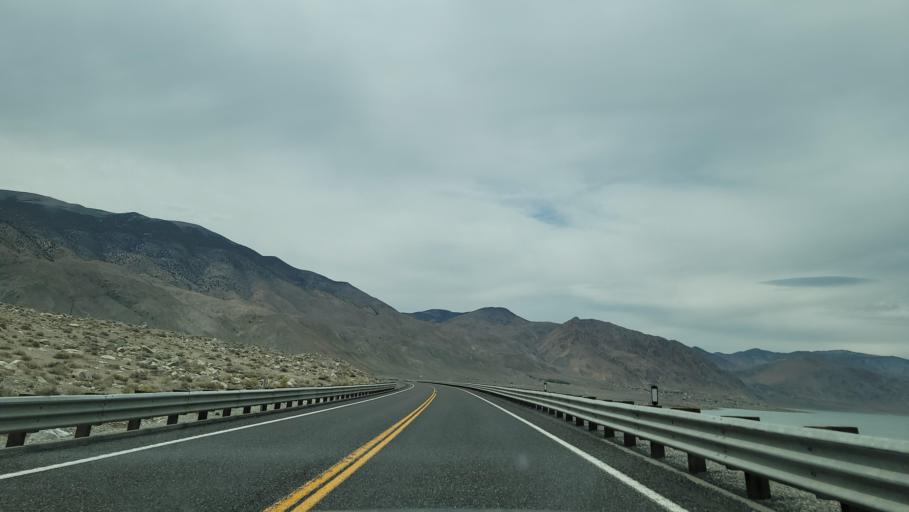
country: US
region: Nevada
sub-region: Mineral County
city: Hawthorne
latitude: 38.6119
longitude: -118.7189
